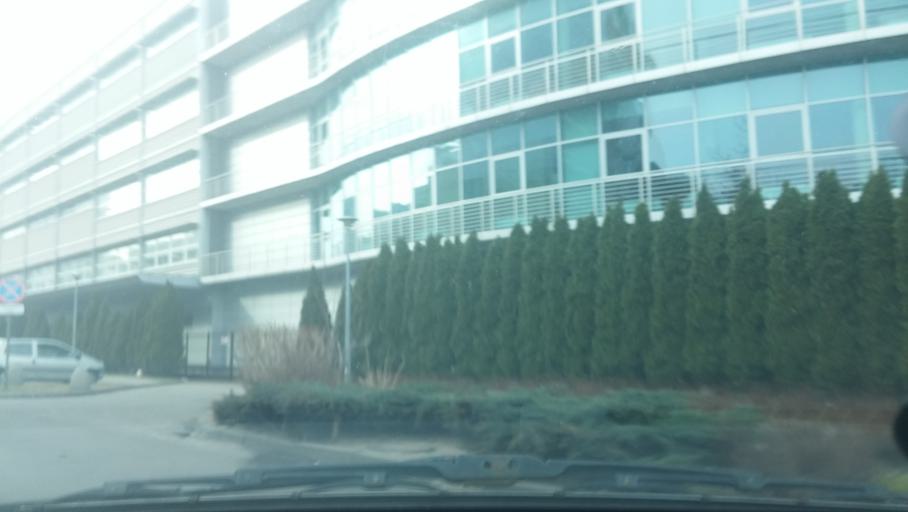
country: PL
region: Masovian Voivodeship
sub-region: Warszawa
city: Praga Poludnie
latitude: 52.2320
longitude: 21.1044
